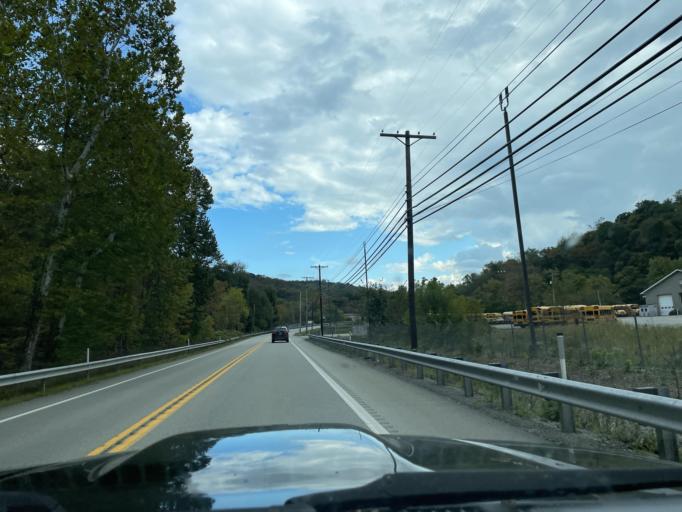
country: US
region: Pennsylvania
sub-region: Westmoreland County
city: Lower Burrell
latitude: 40.5424
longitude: -79.7257
